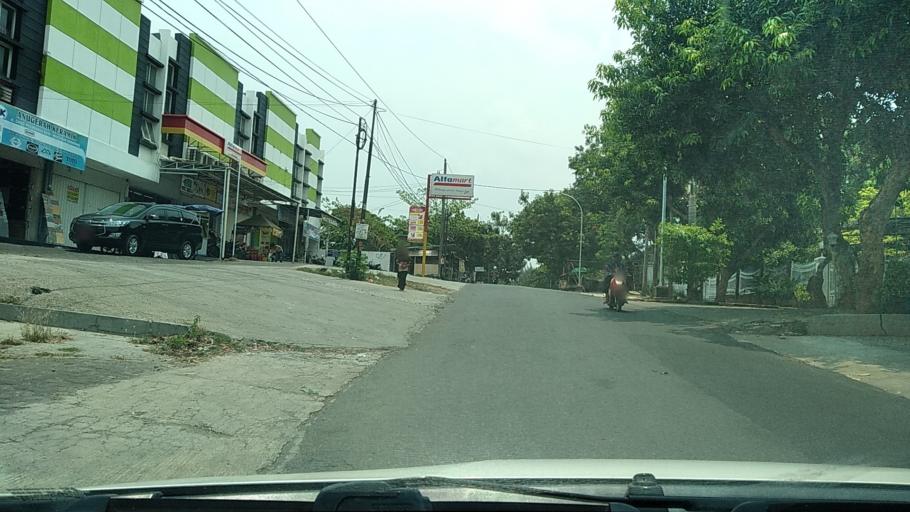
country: ID
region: Central Java
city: Semarang
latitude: -7.0088
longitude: 110.3740
